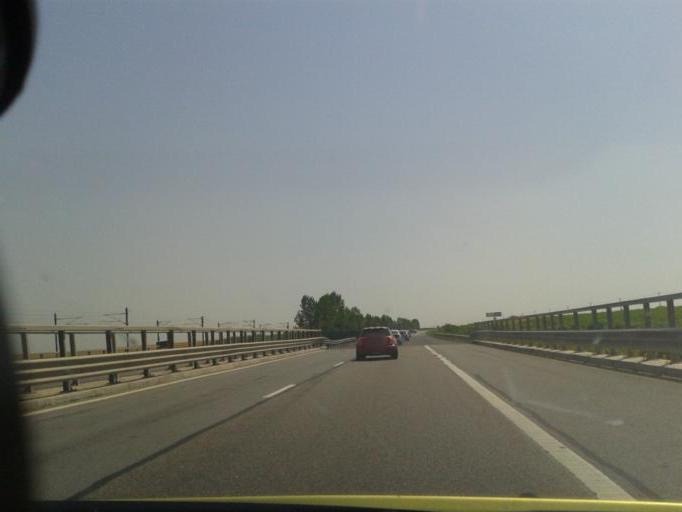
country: RO
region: Calarasi
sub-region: Comuna Tamadau Mare
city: Tamadau Mare
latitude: 44.4471
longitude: 26.5849
